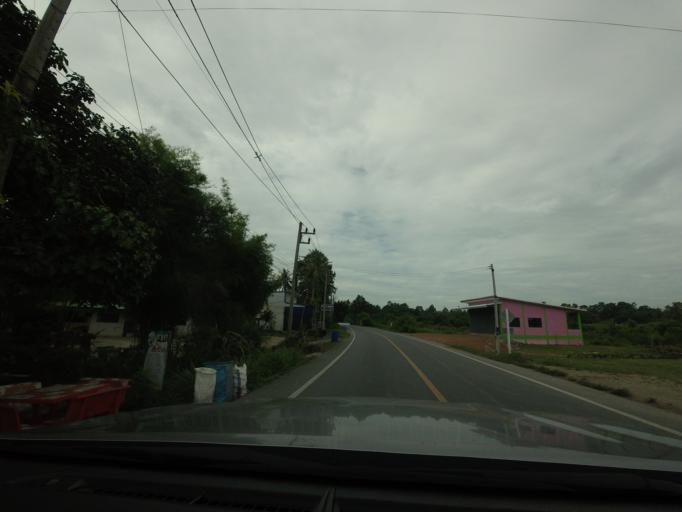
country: TH
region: Nakhon Si Thammarat
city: Phra Phrom
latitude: 8.3124
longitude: 99.9437
